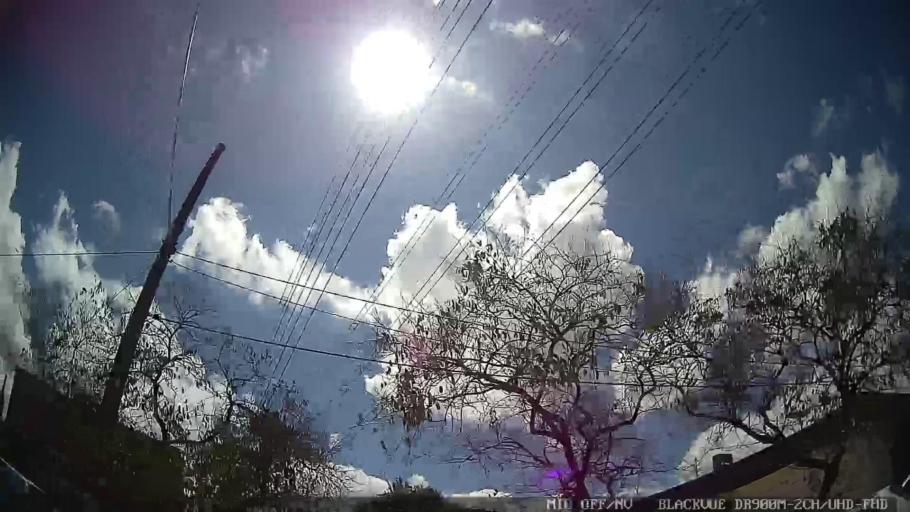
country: BR
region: Sao Paulo
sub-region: Diadema
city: Diadema
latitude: -23.6727
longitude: -46.6057
